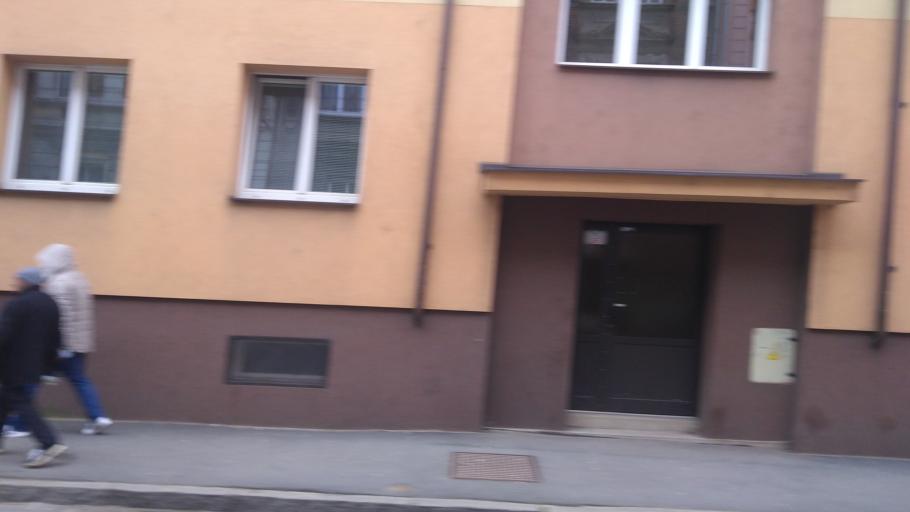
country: CZ
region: Plzensky
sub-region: Okres Plzen-Mesto
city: Pilsen
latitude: 49.7427
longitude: 13.3676
